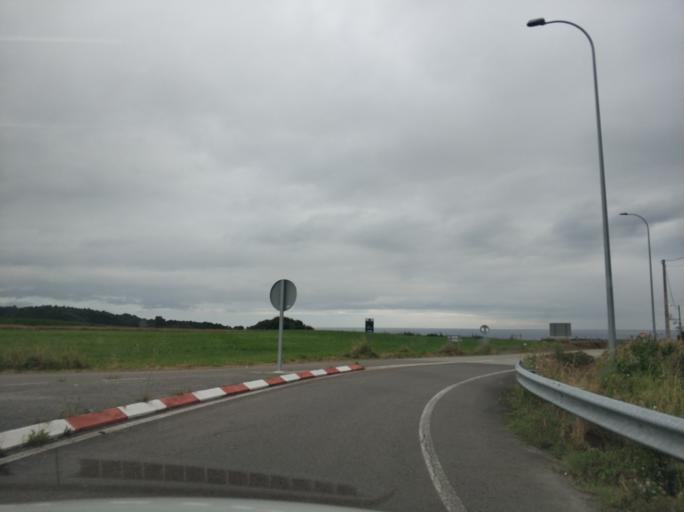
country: ES
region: Galicia
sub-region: Provincia de Lugo
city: Barreiros
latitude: 43.5475
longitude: -7.1517
